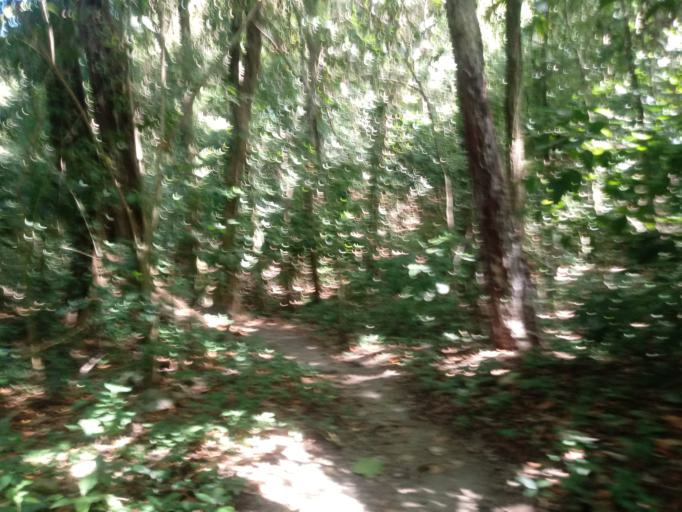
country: CR
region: Puntarenas
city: Paquera
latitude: 9.5832
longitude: -85.0994
